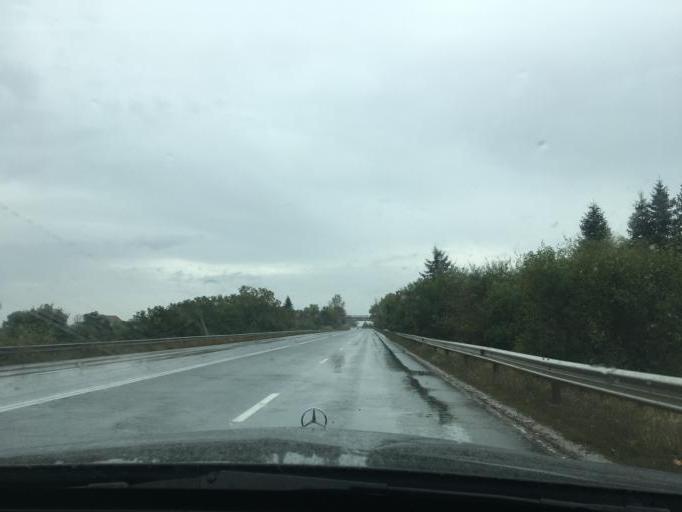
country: BG
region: Sofiya
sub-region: Obshtina Bozhurishte
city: Bozhurishte
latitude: 42.7938
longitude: 23.1481
